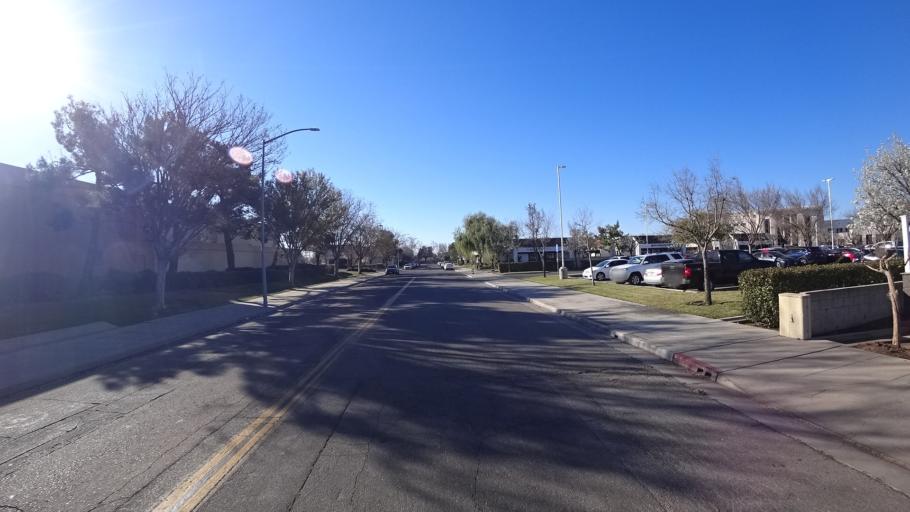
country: US
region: California
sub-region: Fresno County
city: Clovis
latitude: 36.8394
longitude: -119.7567
